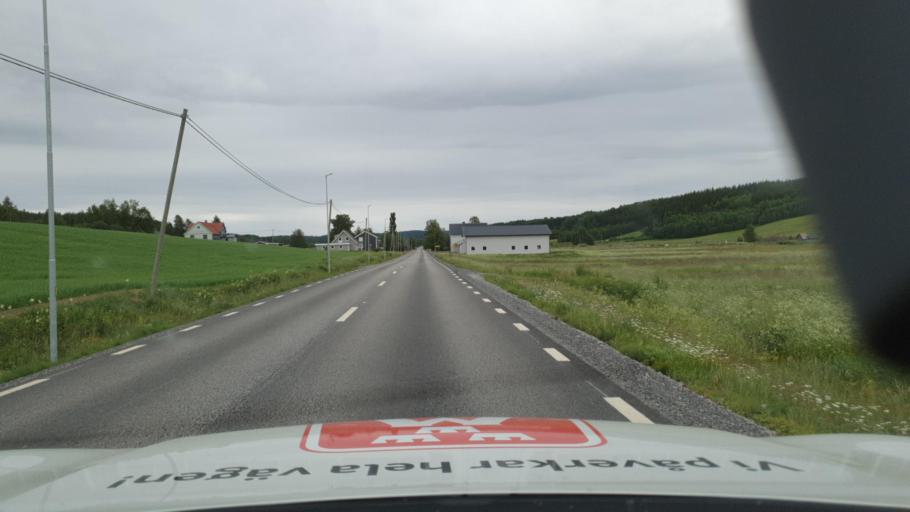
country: SE
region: Vaesterbotten
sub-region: Vannas Kommun
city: Vaennaes
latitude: 63.7624
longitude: 19.6281
